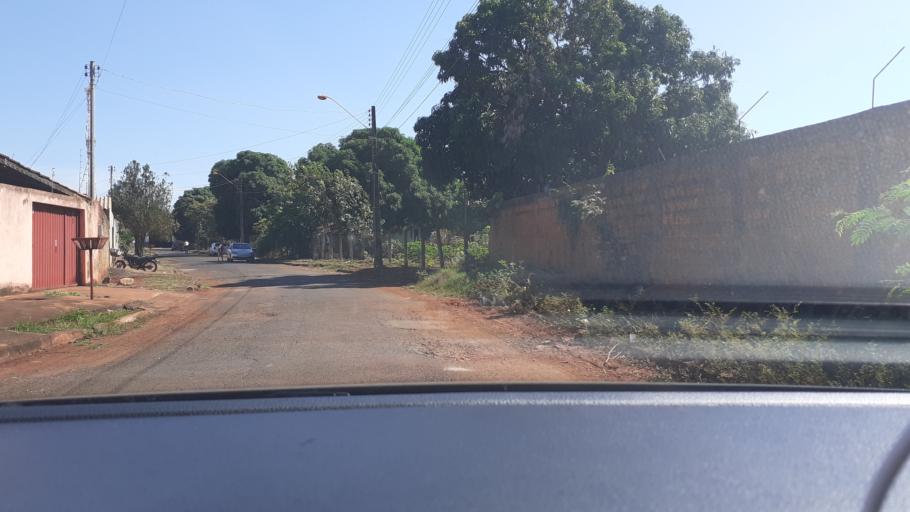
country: BR
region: Goias
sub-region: Itumbiara
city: Itumbiara
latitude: -18.4103
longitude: -49.2547
